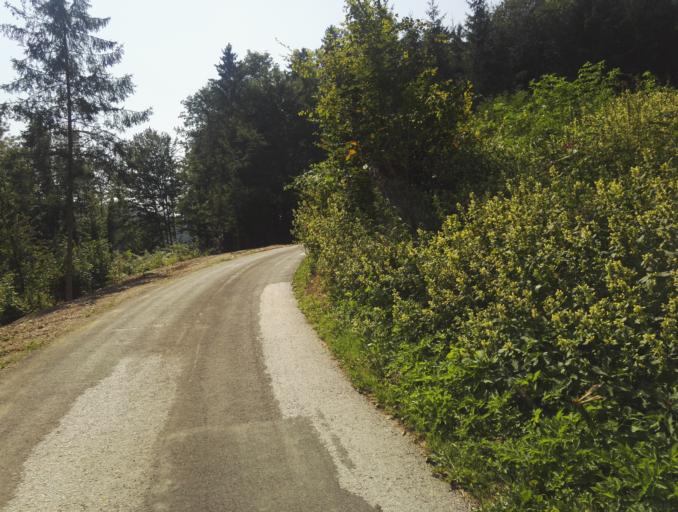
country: AT
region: Styria
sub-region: Politischer Bezirk Graz-Umgebung
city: Eisbach
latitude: 47.1016
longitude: 15.2907
